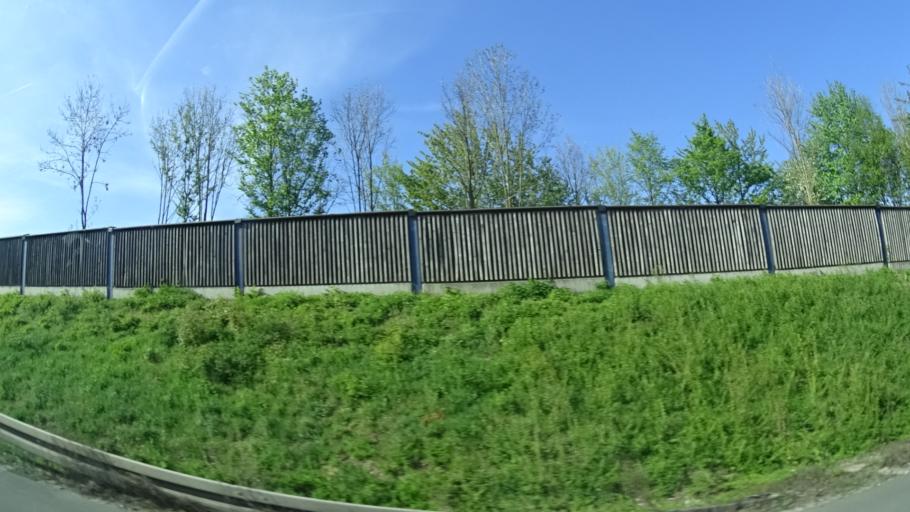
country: DE
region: Bavaria
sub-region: Regierungsbezirk Unterfranken
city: Donnersdorf
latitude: 50.0031
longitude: 10.4211
